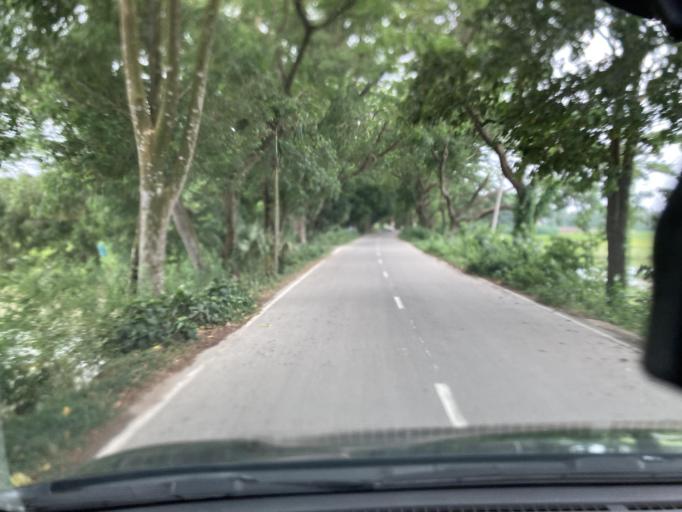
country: BD
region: Dhaka
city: Dohar
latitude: 23.7868
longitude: 90.0640
